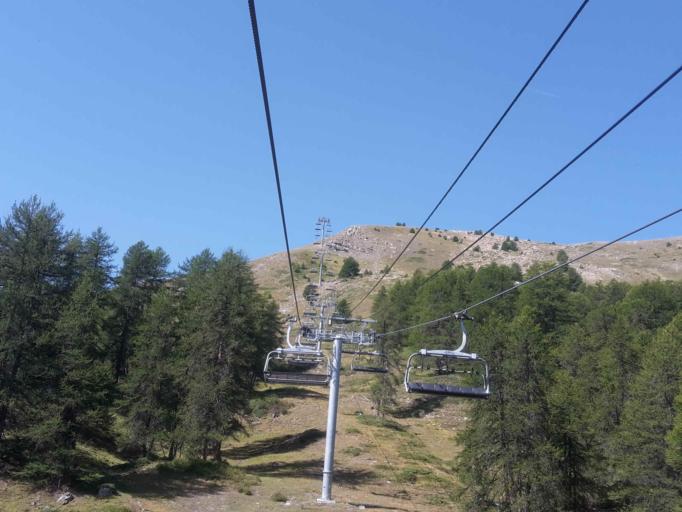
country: FR
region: Provence-Alpes-Cote d'Azur
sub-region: Departement des Hautes-Alpes
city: Guillestre
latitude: 44.5907
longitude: 6.6675
